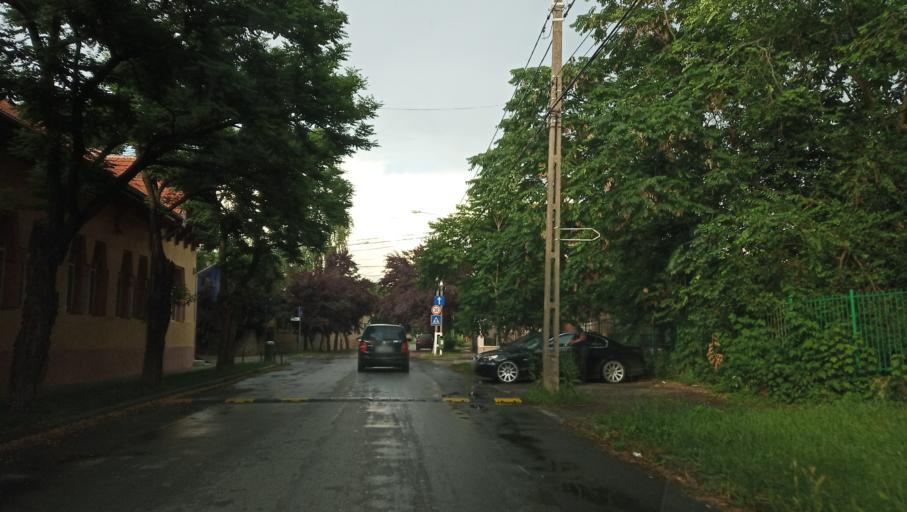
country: RO
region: Timis
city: Timisoara
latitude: 45.7388
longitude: 21.2304
